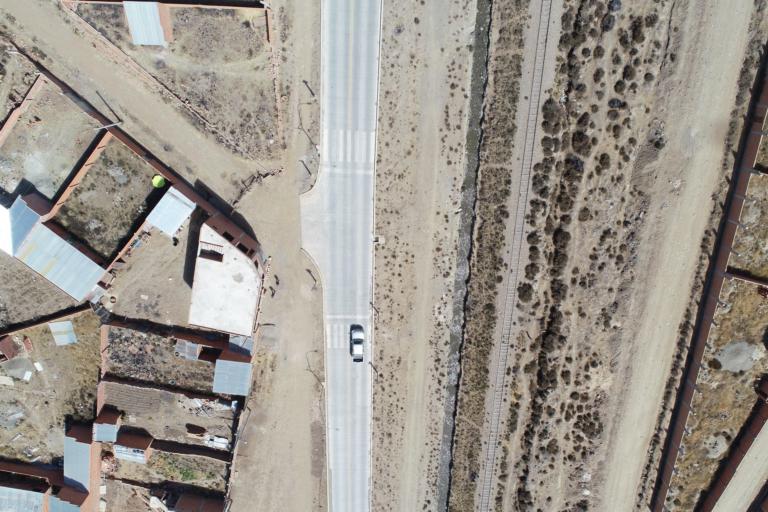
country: BO
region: La Paz
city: La Paz
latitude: -16.5921
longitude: -68.2142
